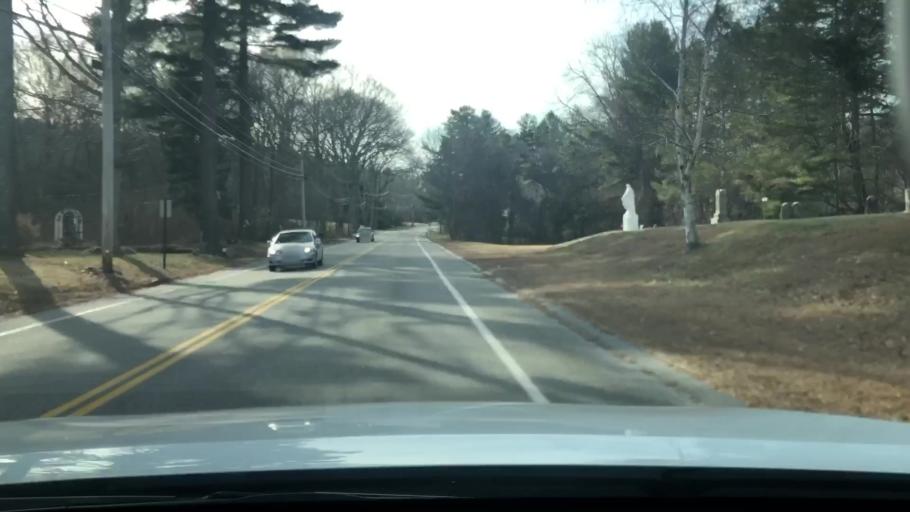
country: US
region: Massachusetts
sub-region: Worcester County
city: Grafton
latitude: 42.2027
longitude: -71.7025
